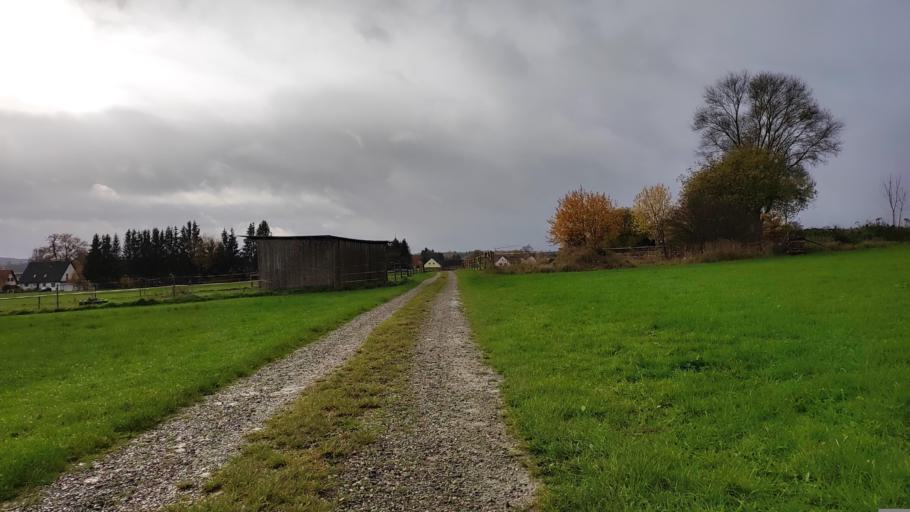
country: DE
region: Bavaria
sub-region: Swabia
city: Dinkelscherben
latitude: 48.3436
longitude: 10.5502
